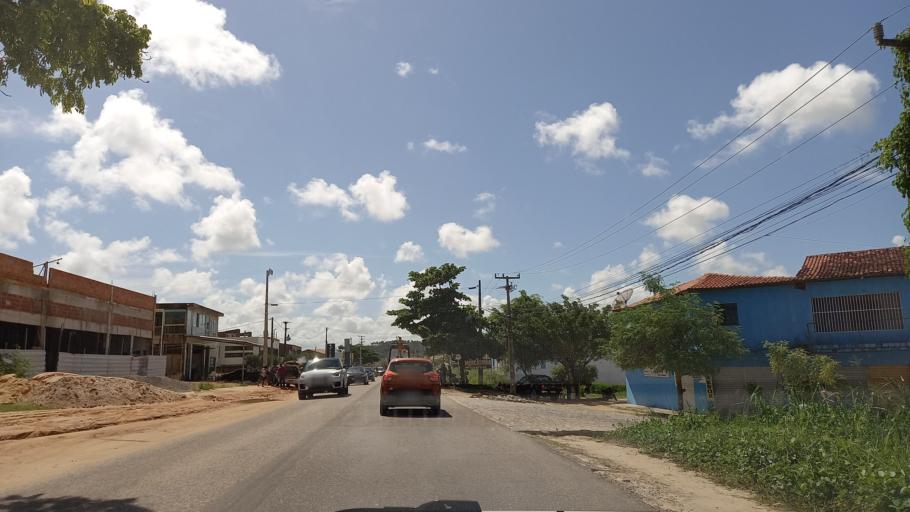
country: BR
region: Pernambuco
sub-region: Sao Jose Da Coroa Grande
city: Sao Jose da Coroa Grande
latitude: -8.8895
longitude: -35.1514
